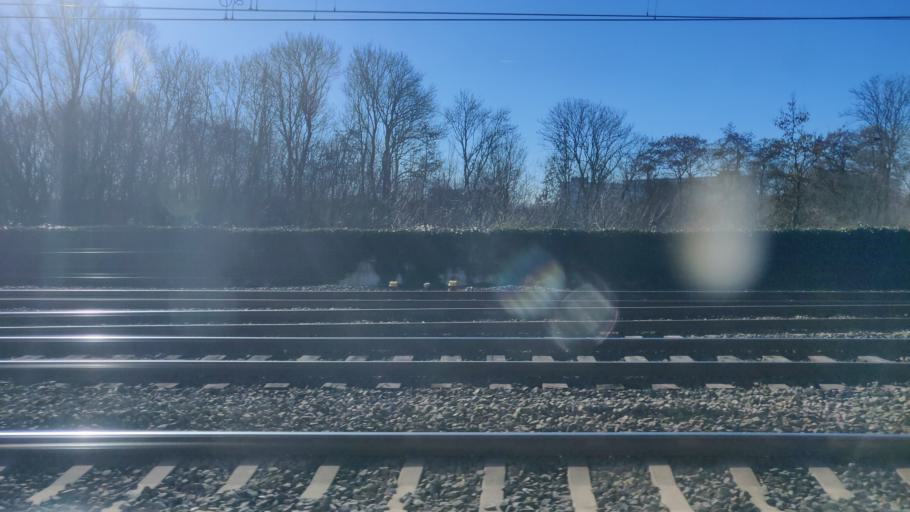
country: NL
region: North Holland
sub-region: Gemeente Weesp
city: Weesp
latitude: 52.3176
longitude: 5.0336
